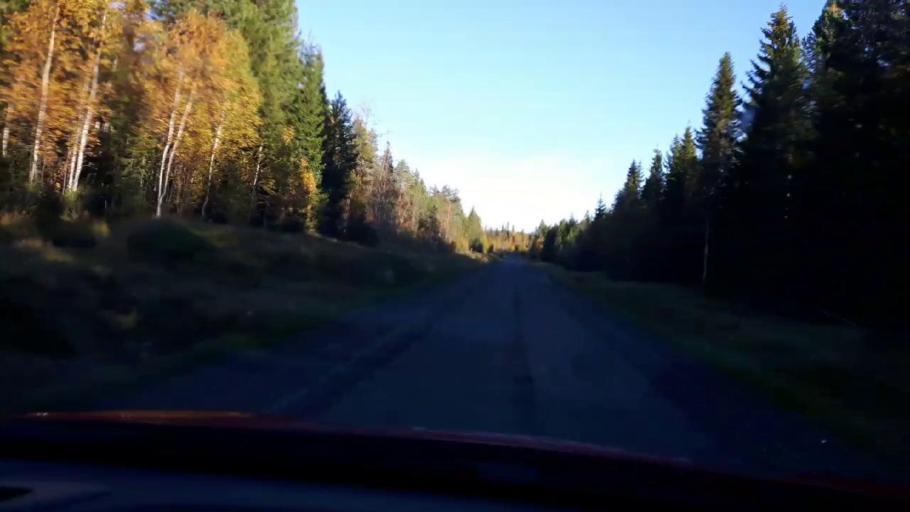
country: SE
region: Jaemtland
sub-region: OEstersunds Kommun
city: Lit
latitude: 63.5962
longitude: 14.8280
